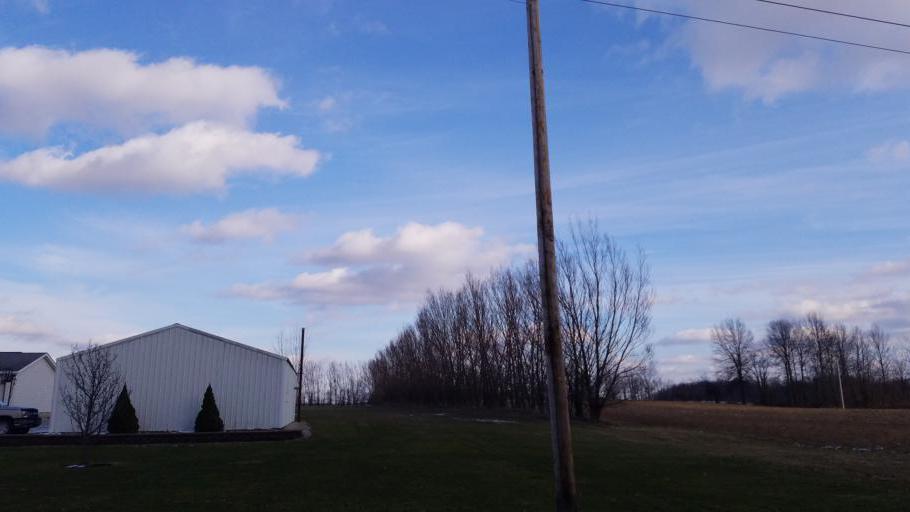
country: US
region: Ohio
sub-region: Crawford County
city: Galion
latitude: 40.6564
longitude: -82.7185
